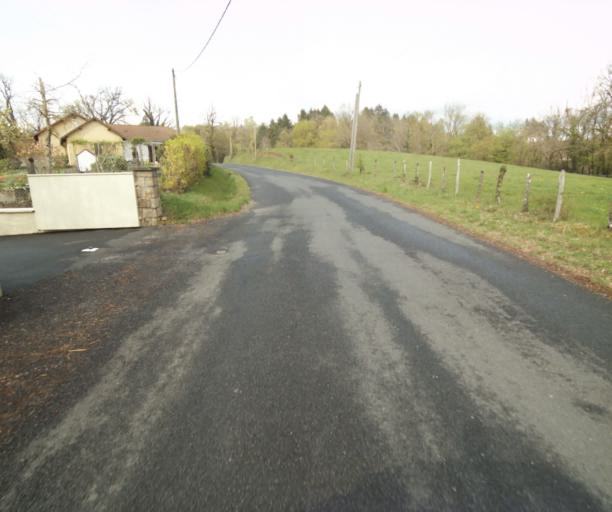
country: FR
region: Limousin
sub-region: Departement de la Correze
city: Tulle
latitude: 45.2681
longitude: 1.7506
